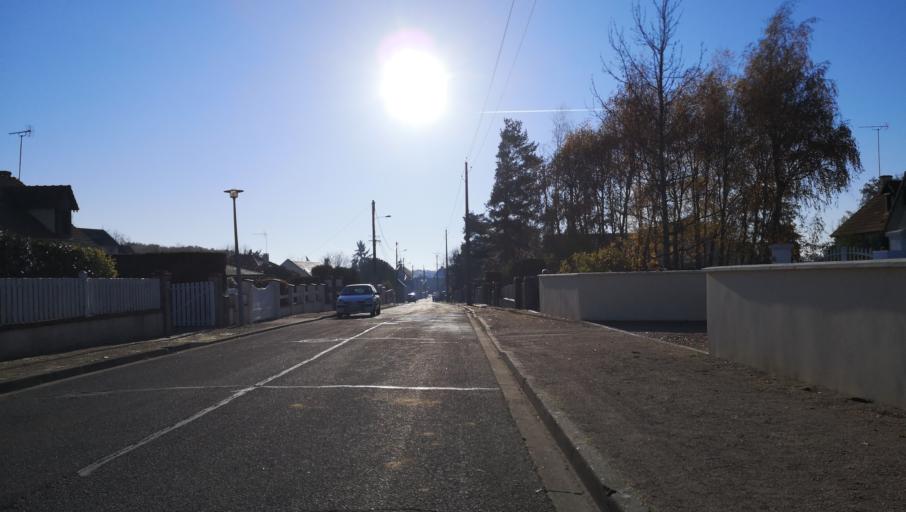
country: FR
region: Centre
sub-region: Departement du Loiret
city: Saint-Jean-de-la-Ruelle
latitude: 47.9353
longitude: 1.8520
